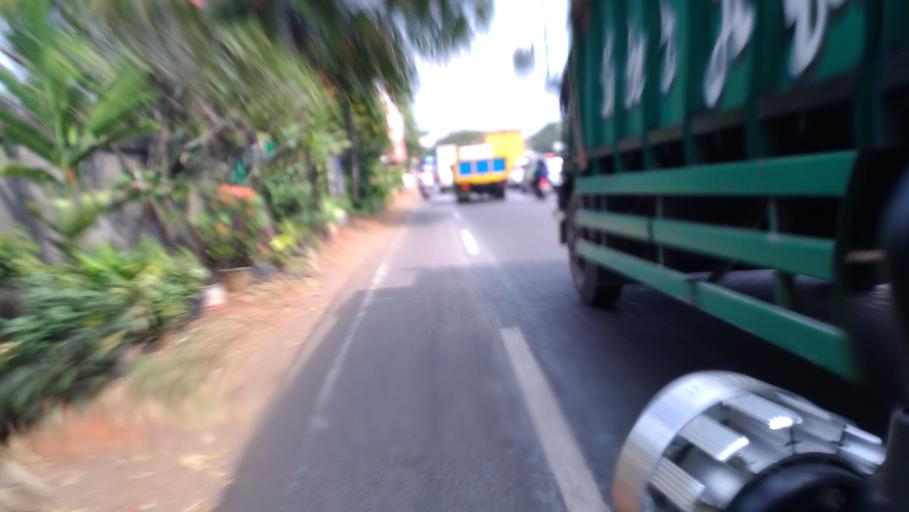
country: ID
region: West Java
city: Cileungsir
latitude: -6.3731
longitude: 106.8967
